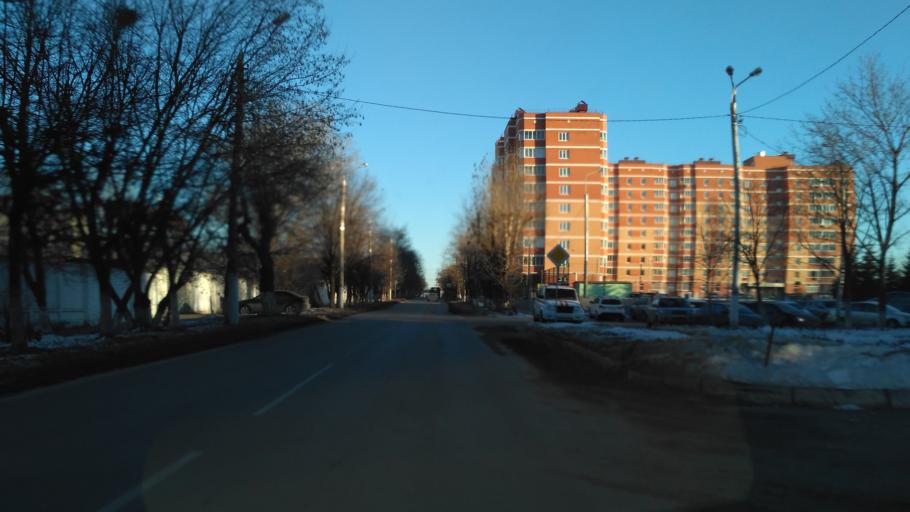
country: RU
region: Tula
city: Tula
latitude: 54.2098
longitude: 37.6114
